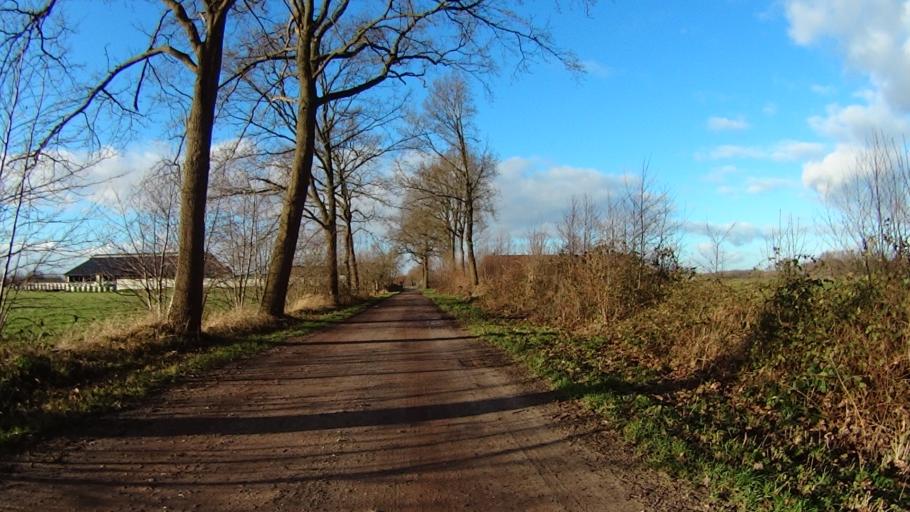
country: NL
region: Gelderland
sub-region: Gemeente Barneveld
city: Terschuur
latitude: 52.1751
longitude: 5.5171
